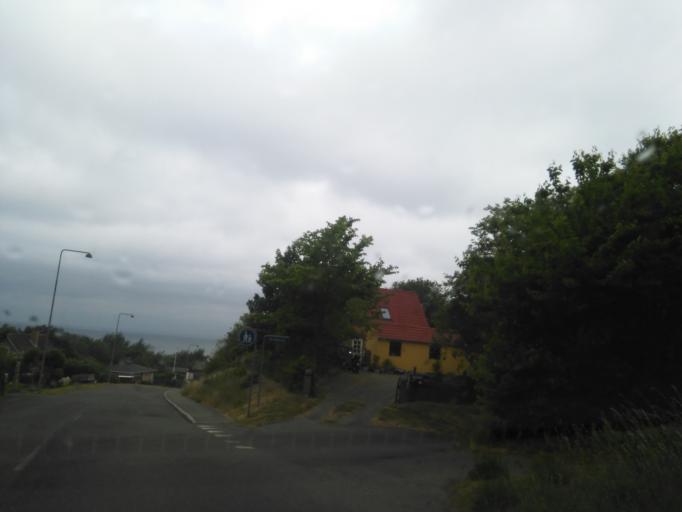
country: DK
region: Capital Region
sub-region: Bornholm Kommune
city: Ronne
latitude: 55.2468
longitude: 14.7404
